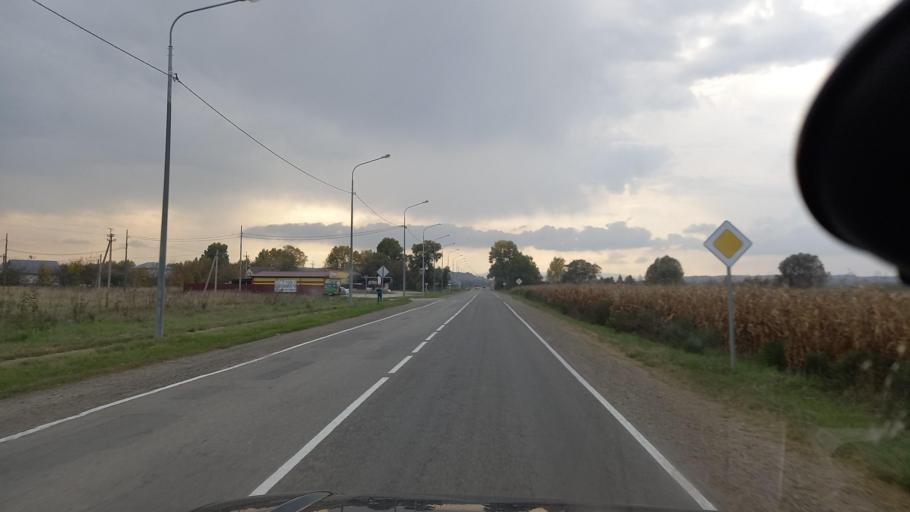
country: RU
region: Krasnodarskiy
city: Mostovskoy
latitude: 44.3976
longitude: 40.7736
